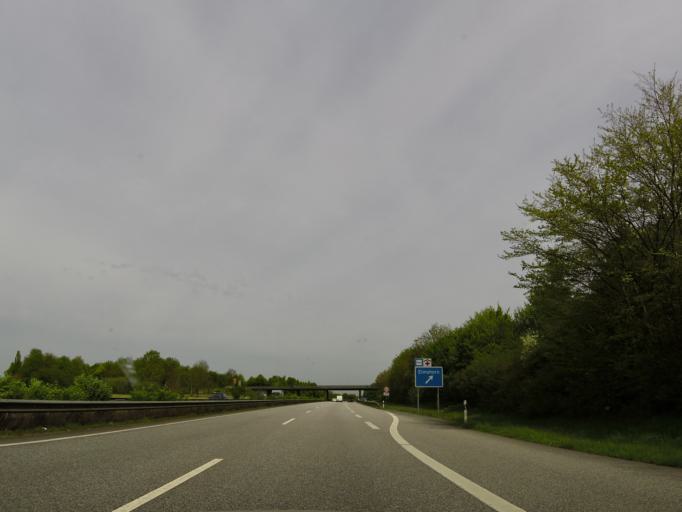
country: DE
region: Schleswig-Holstein
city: Seeth-Ekholt
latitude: 53.7419
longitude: 9.7139
